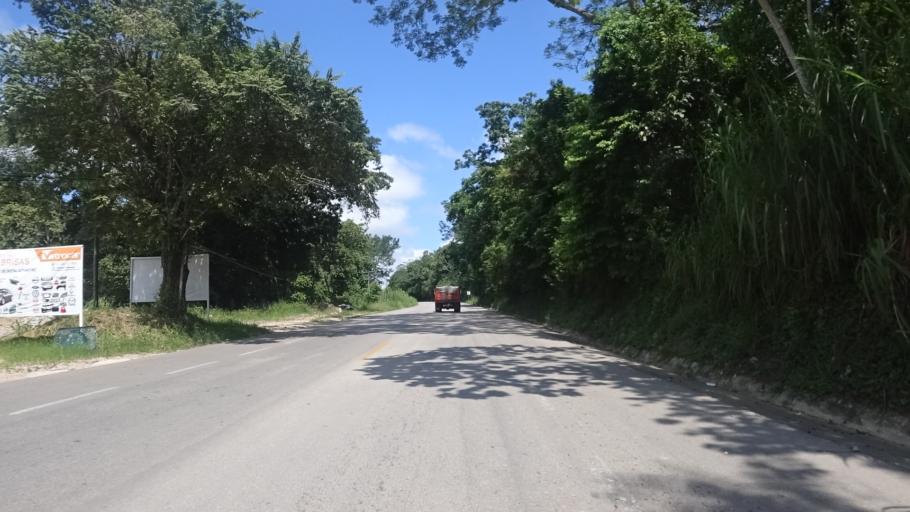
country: MX
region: Chiapas
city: Palenque
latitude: 17.4975
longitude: -91.9877
